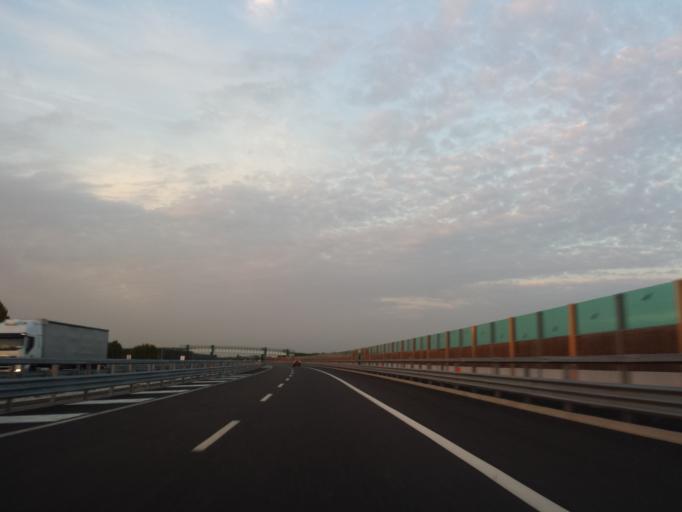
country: IT
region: Veneto
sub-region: Provincia di Padova
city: Bastia
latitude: 45.3986
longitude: 11.6276
